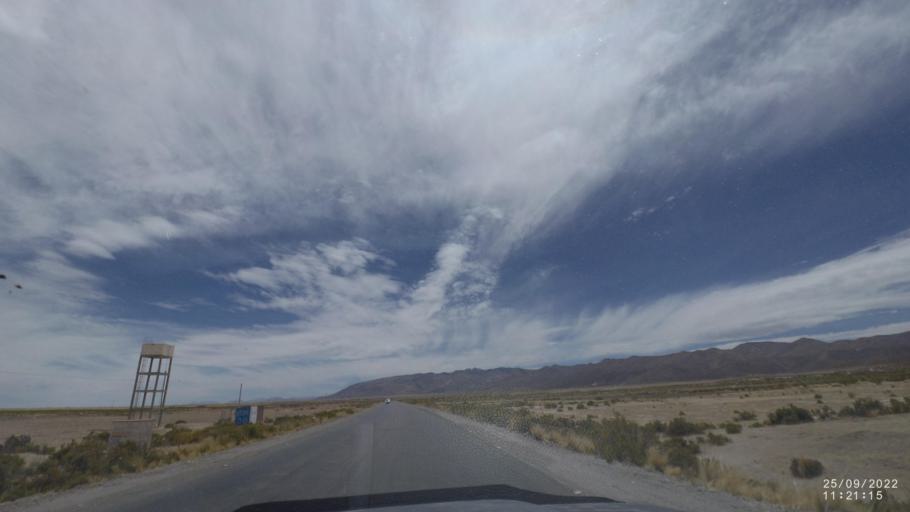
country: BO
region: Oruro
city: Challapata
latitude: -19.1465
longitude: -66.7712
